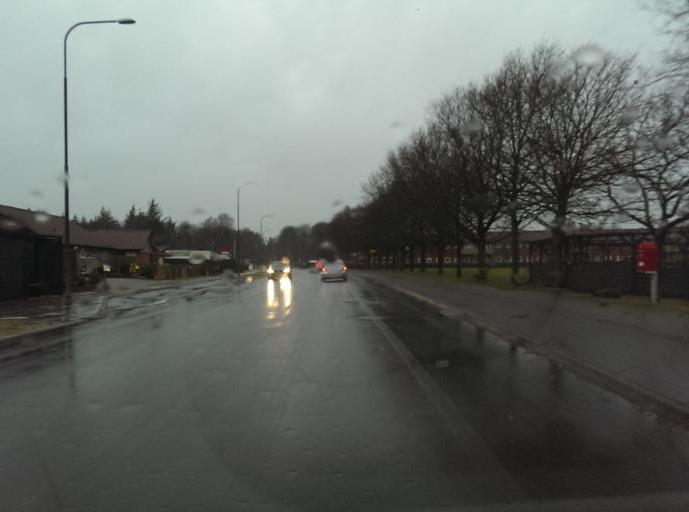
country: DK
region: South Denmark
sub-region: Esbjerg Kommune
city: Esbjerg
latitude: 55.4965
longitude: 8.4465
